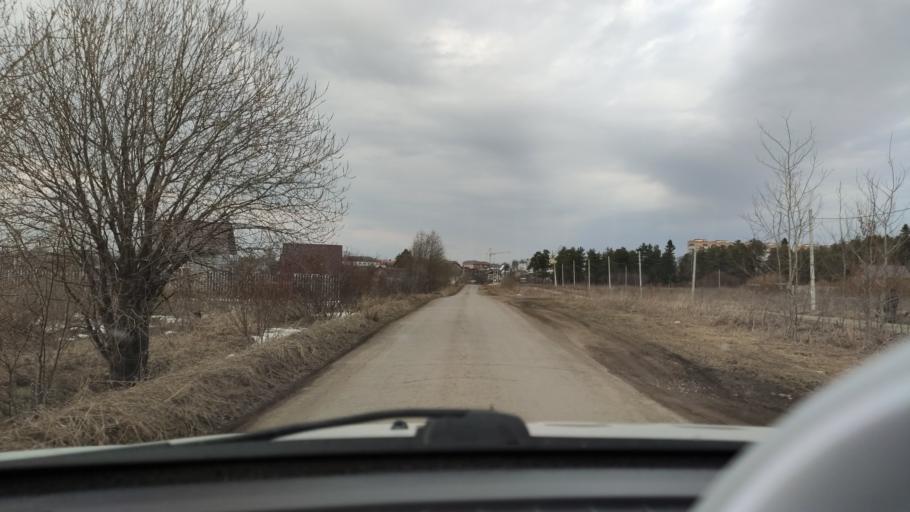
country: RU
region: Perm
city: Ferma
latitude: 57.8889
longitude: 56.3283
